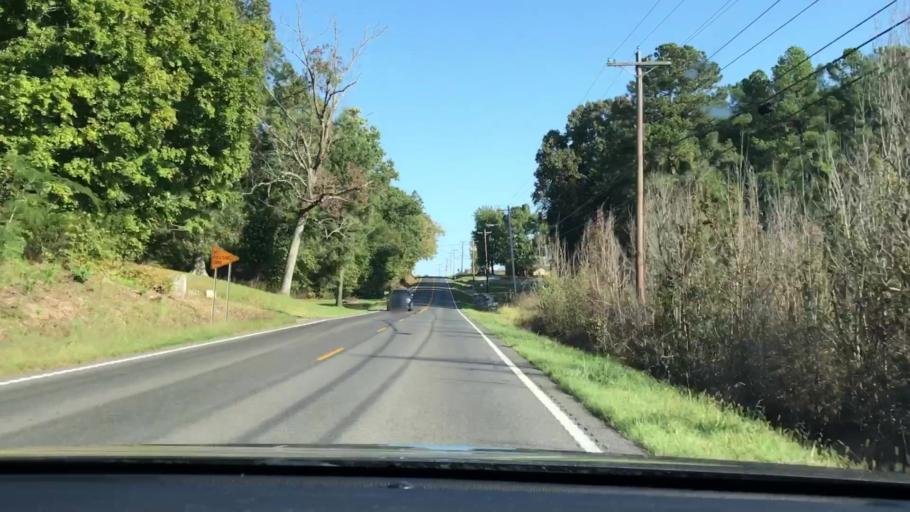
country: US
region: Kentucky
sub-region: Marshall County
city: Benton
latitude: 36.8252
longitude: -88.3506
